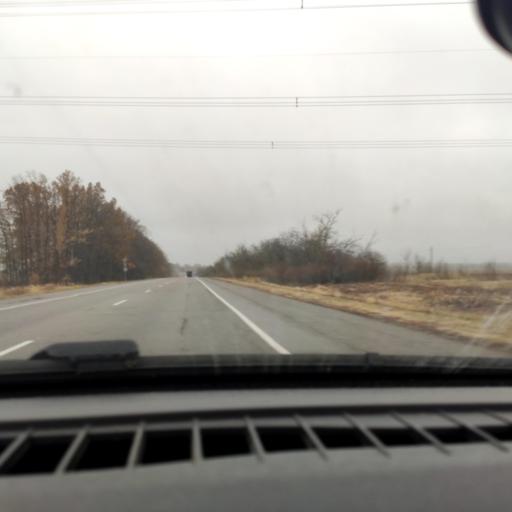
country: RU
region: Voronezj
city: Kolodeznyy
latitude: 51.3280
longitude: 39.0269
